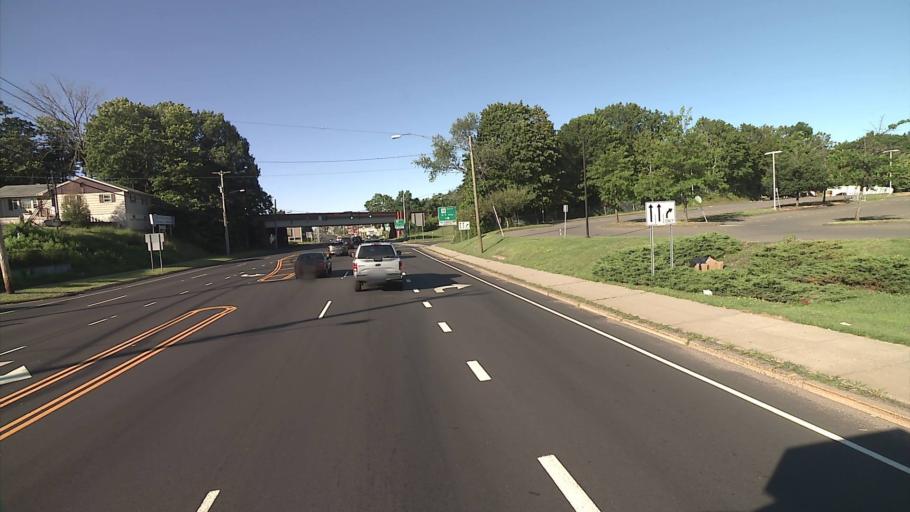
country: US
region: Connecticut
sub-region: New Haven County
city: Hamden
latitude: 41.3668
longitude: -72.9211
